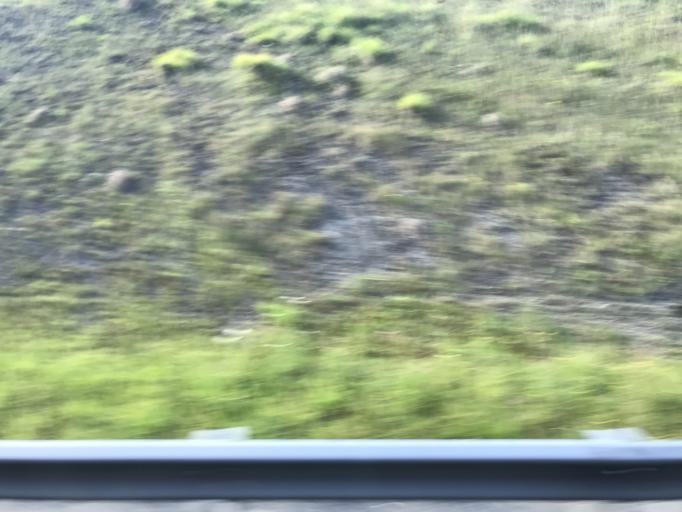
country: ES
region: Basque Country
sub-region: Provincia de Guipuzcoa
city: Andoain
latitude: 43.2280
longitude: -2.0153
